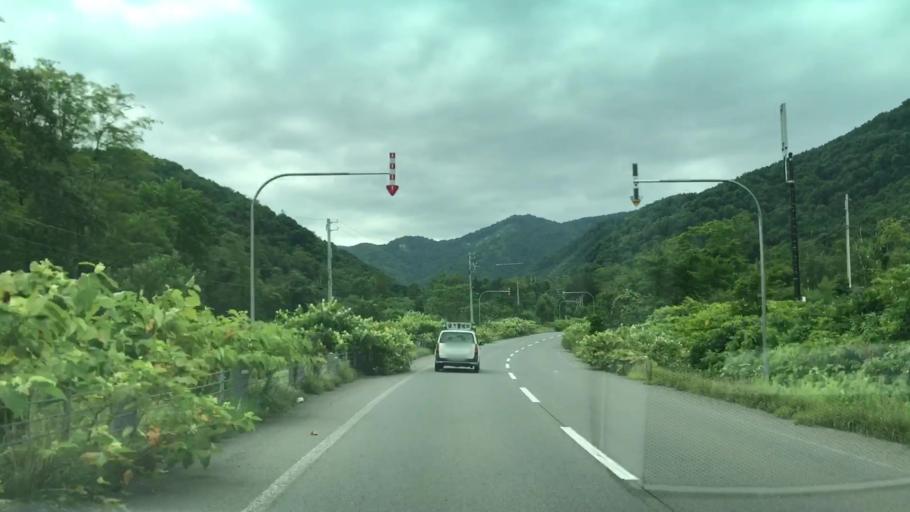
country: JP
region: Hokkaido
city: Yoichi
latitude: 43.0263
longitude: 140.8665
